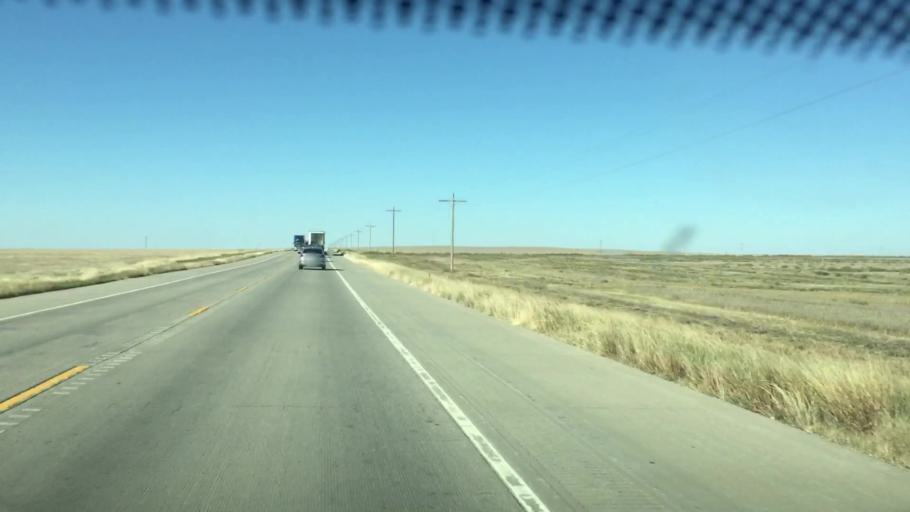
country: US
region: Colorado
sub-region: Prowers County
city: Lamar
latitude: 38.2503
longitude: -102.7240
